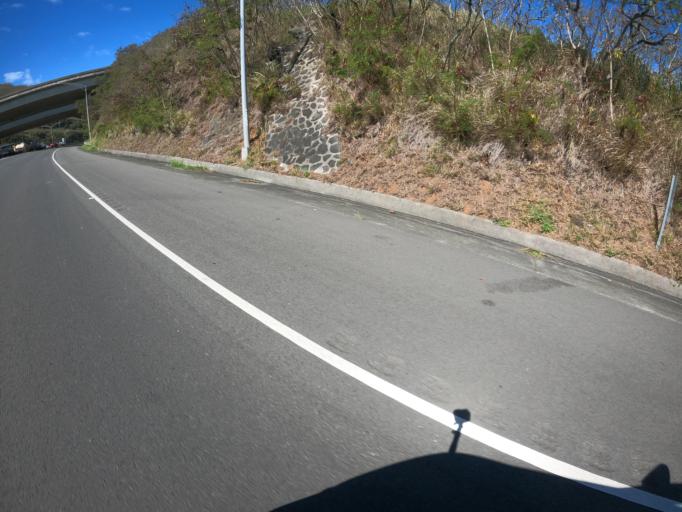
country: US
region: Hawaii
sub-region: Honolulu County
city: Kailua
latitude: 21.4065
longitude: -157.7652
